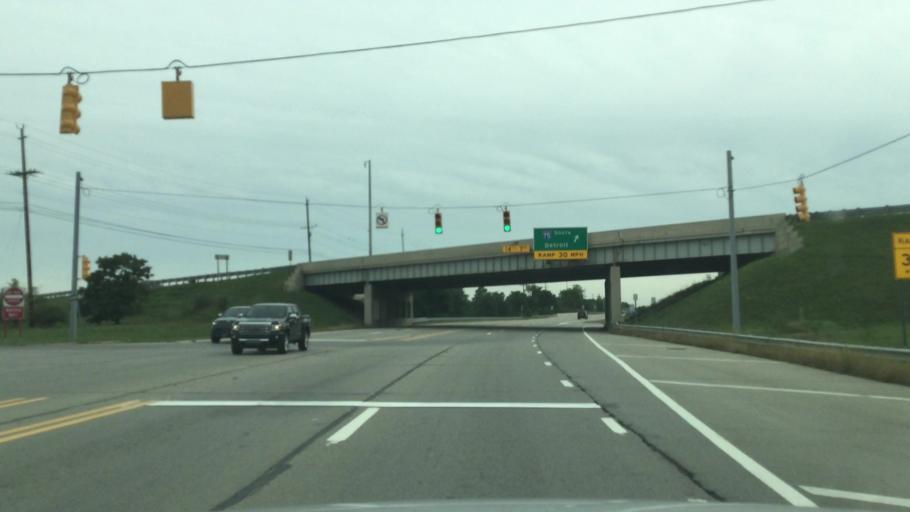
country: US
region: Michigan
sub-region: Oakland County
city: Clarkston
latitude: 42.7410
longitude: -83.4545
